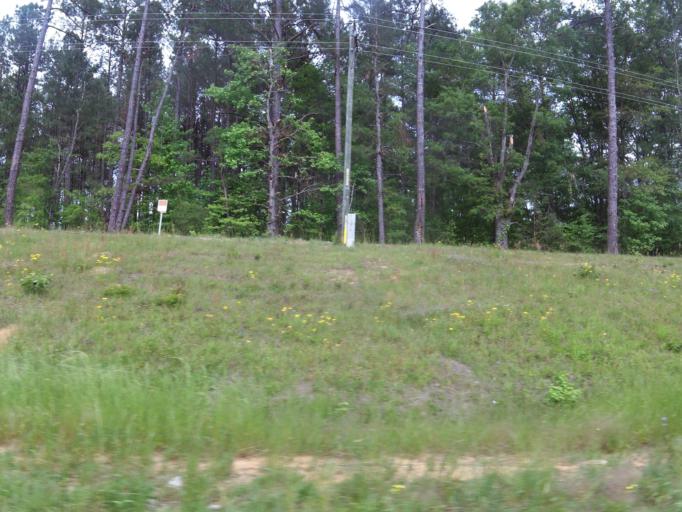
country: US
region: Georgia
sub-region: McDuffie County
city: Thomson
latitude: 33.3440
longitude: -82.4590
